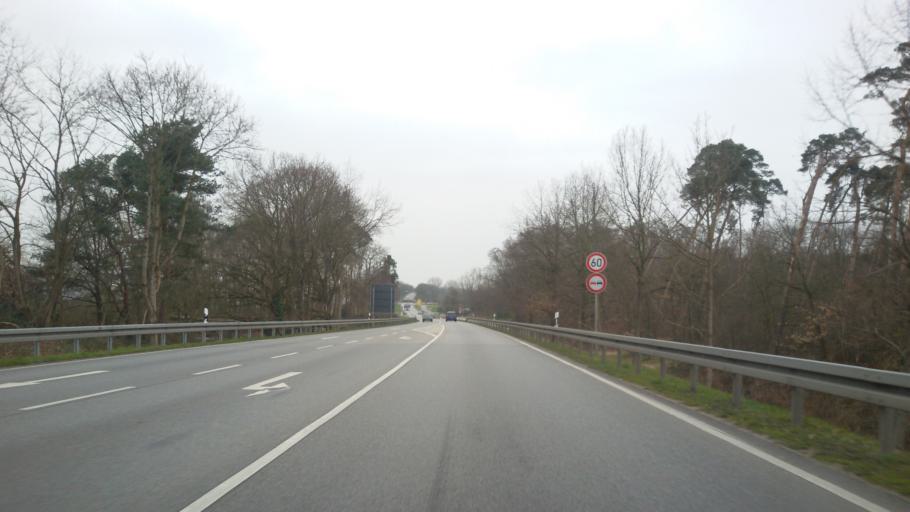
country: DE
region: Hesse
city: Lorsch
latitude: 49.6653
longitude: 8.5684
